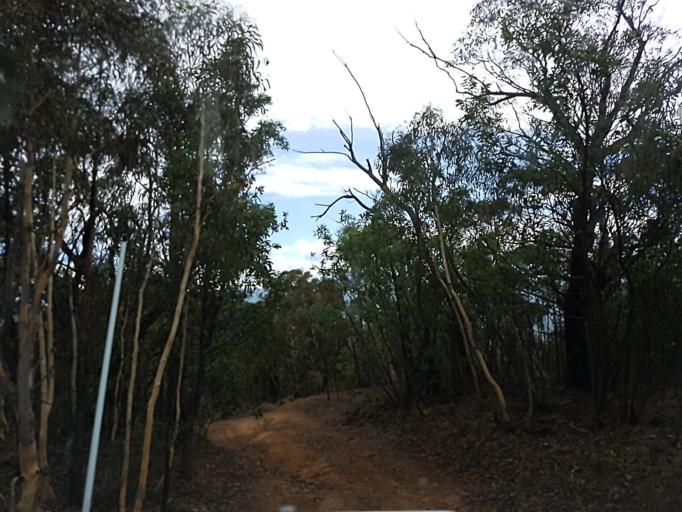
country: AU
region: New South Wales
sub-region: Snowy River
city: Jindabyne
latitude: -36.9050
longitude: 148.3416
